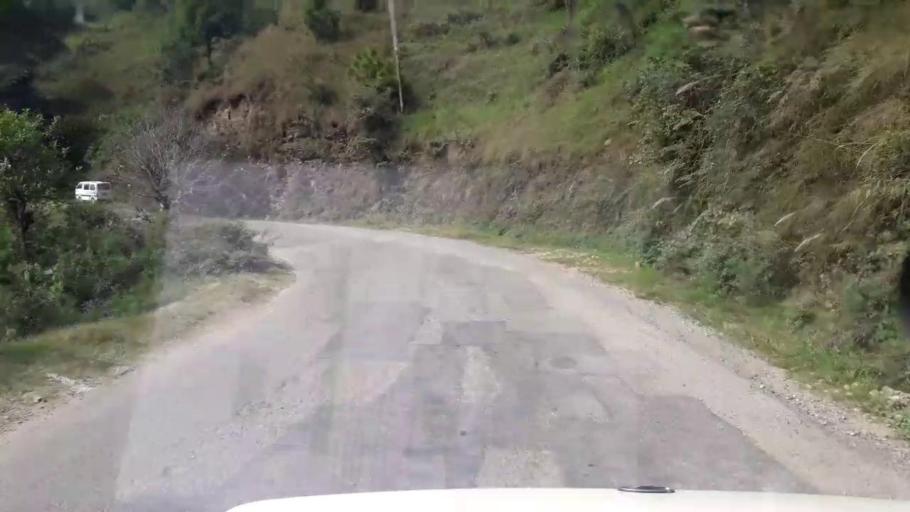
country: IN
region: Himachal Pradesh
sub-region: Shimla
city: Shimla
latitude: 31.0479
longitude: 77.1486
